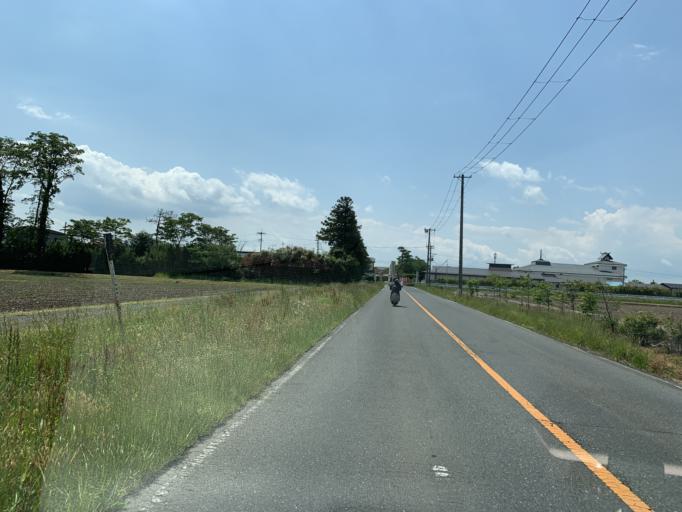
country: JP
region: Miyagi
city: Kogota
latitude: 38.5873
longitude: 141.0315
